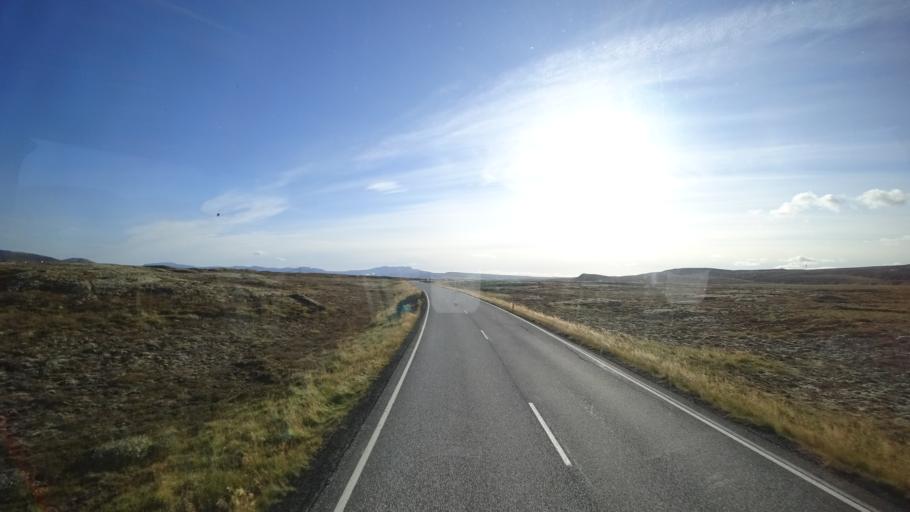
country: IS
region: South
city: Hveragerdi
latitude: 64.2665
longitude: -21.1264
